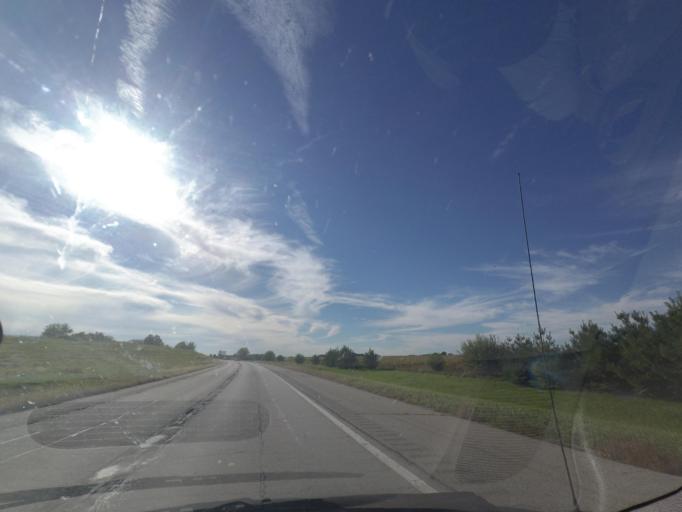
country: US
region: Illinois
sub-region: Macon County
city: Forsyth
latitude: 39.9083
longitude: -88.9828
